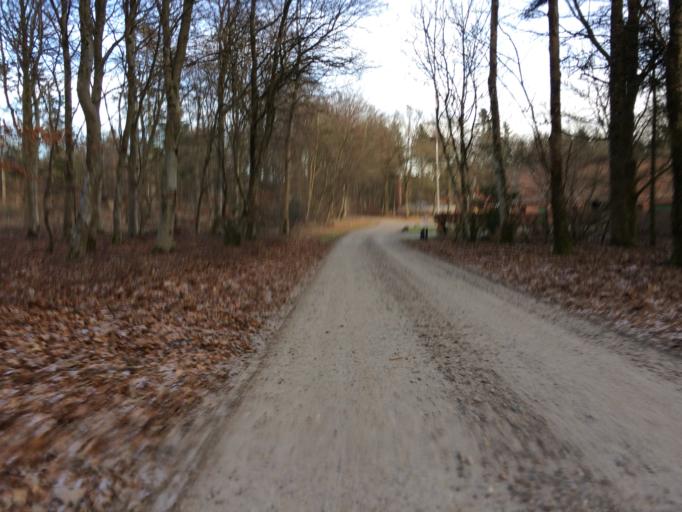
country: DK
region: Central Jutland
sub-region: Holstebro Kommune
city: Ulfborg
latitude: 56.2533
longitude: 8.4645
